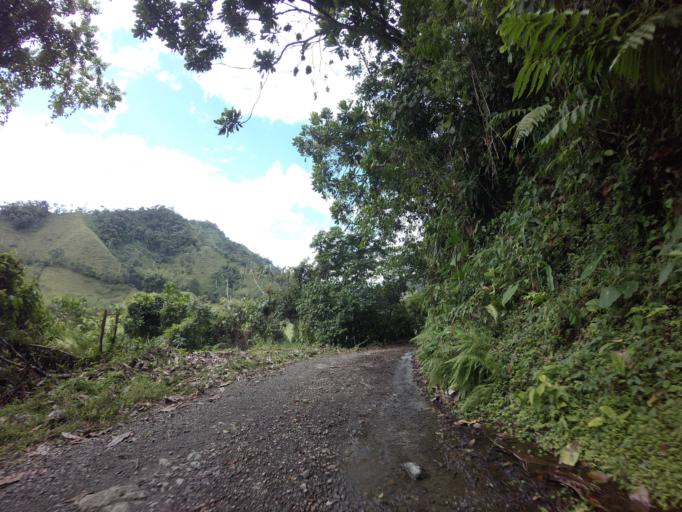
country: CO
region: Antioquia
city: Narino
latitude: 5.5306
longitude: -75.1485
